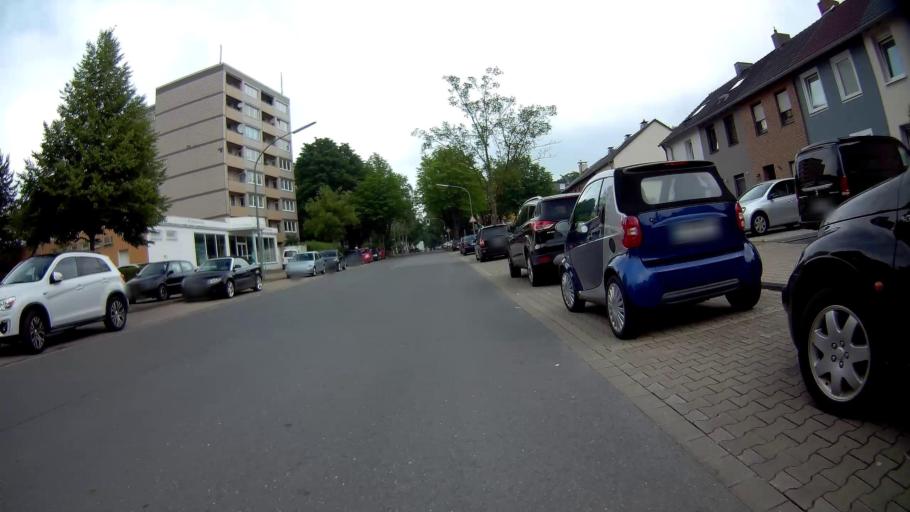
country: DE
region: North Rhine-Westphalia
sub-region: Regierungsbezirk Munster
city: Gladbeck
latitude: 51.5621
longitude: 7.0260
